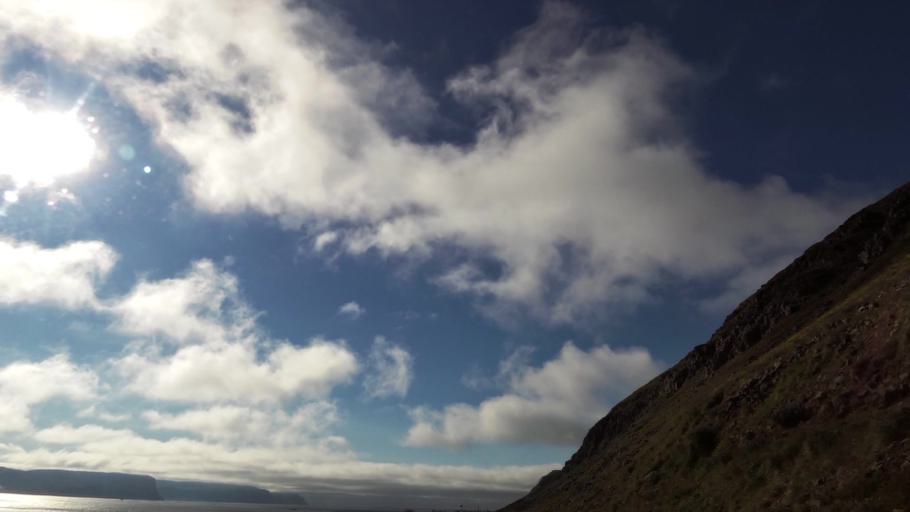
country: IS
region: West
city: Olafsvik
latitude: 65.5675
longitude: -23.9256
